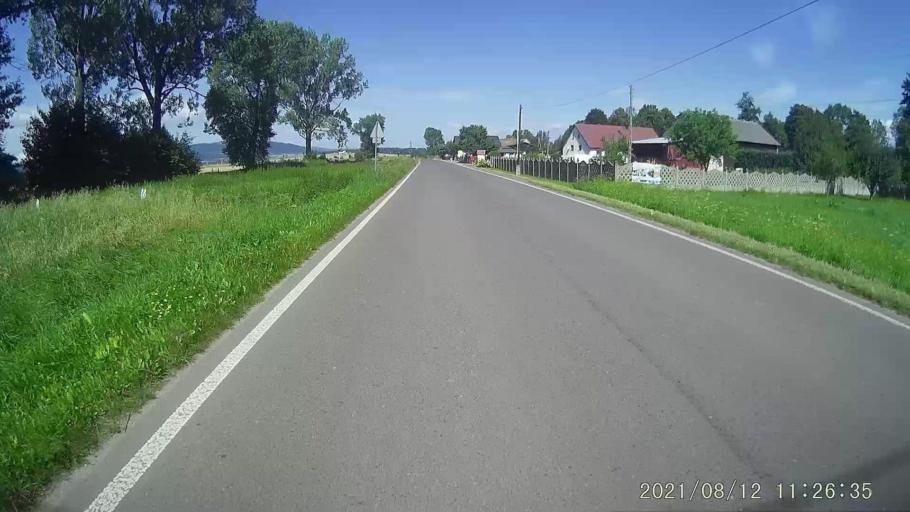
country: PL
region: Lower Silesian Voivodeship
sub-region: Powiat klodzki
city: Bystrzyca Klodzka
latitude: 50.2755
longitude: 16.6866
